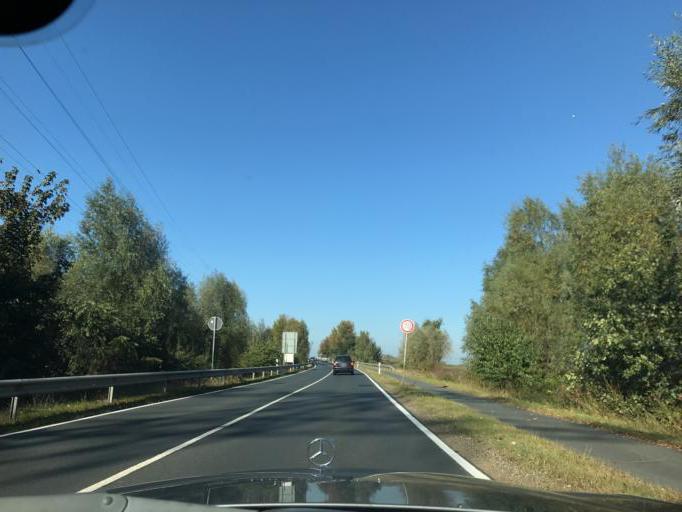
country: DE
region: Lower Saxony
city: Papenburg
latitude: 53.0992
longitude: 7.3541
